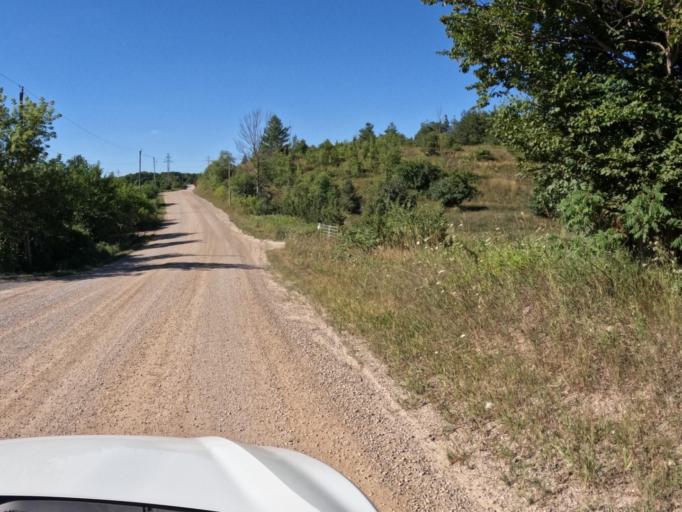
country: CA
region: Ontario
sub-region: Wellington County
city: Guelph
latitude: 43.4234
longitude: -80.1247
